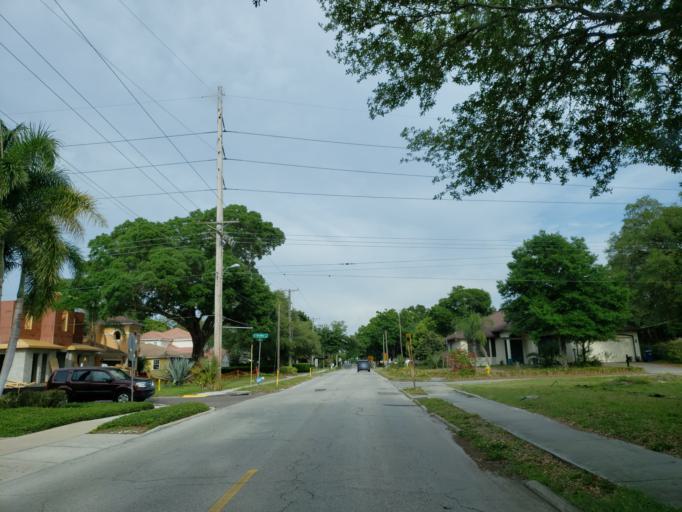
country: US
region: Florida
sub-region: Hillsborough County
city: Tampa
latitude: 27.9376
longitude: -82.5103
